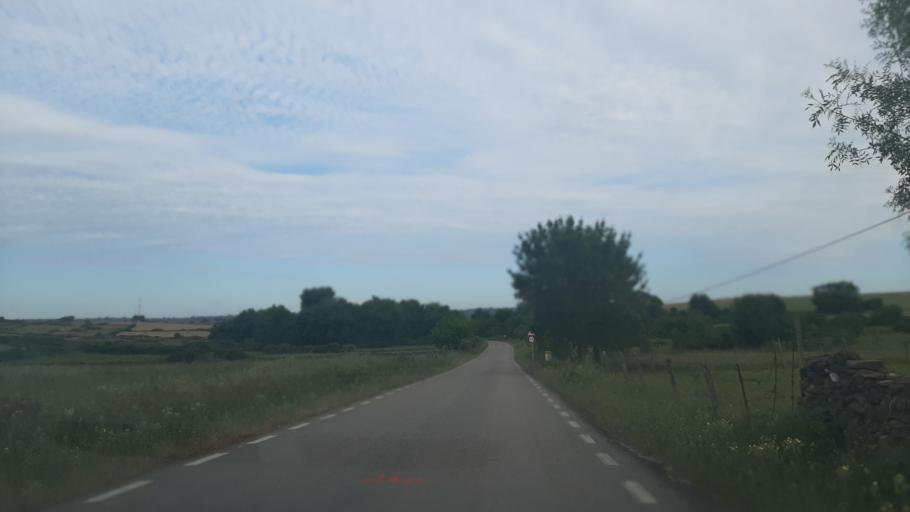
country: ES
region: Castille and Leon
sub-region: Provincia de Salamanca
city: Gallegos de Arganan
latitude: 40.6457
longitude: -6.7472
